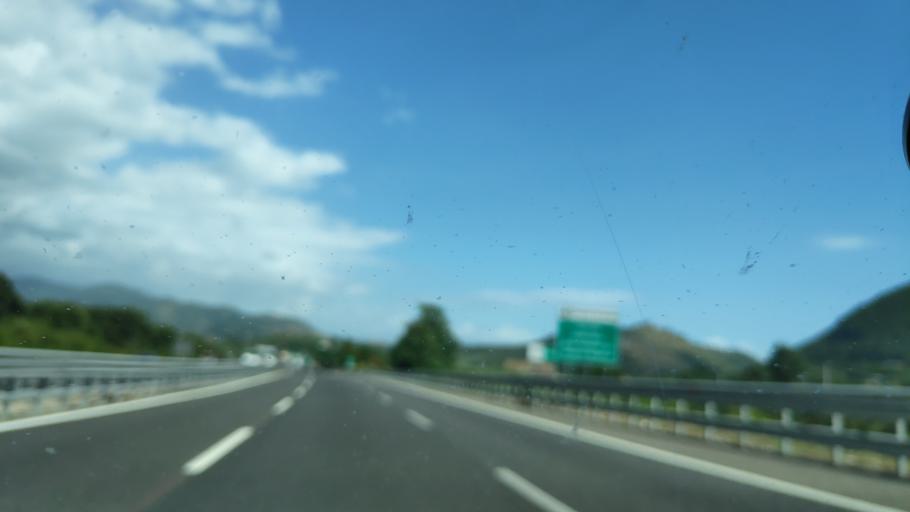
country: IT
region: Campania
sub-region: Provincia di Salerno
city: San Mango Piemonte
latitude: 40.6879
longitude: 14.8425
